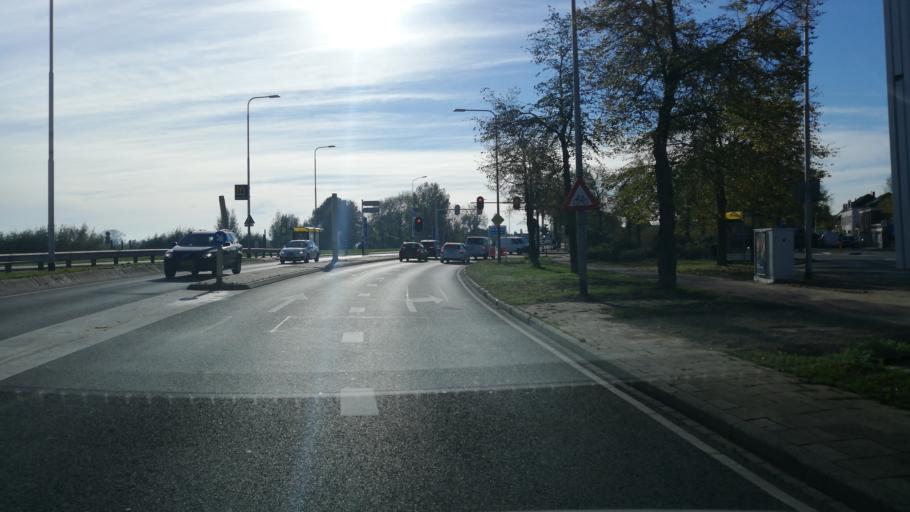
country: NL
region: Gelderland
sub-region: Gemeente Zutphen
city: Zutphen
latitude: 52.1415
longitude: 6.1847
